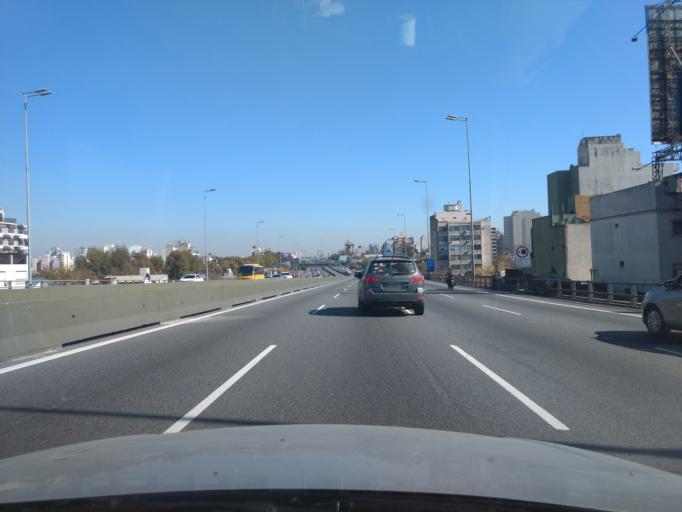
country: AR
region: Buenos Aires F.D.
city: Buenos Aires
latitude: -34.6267
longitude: -58.4085
